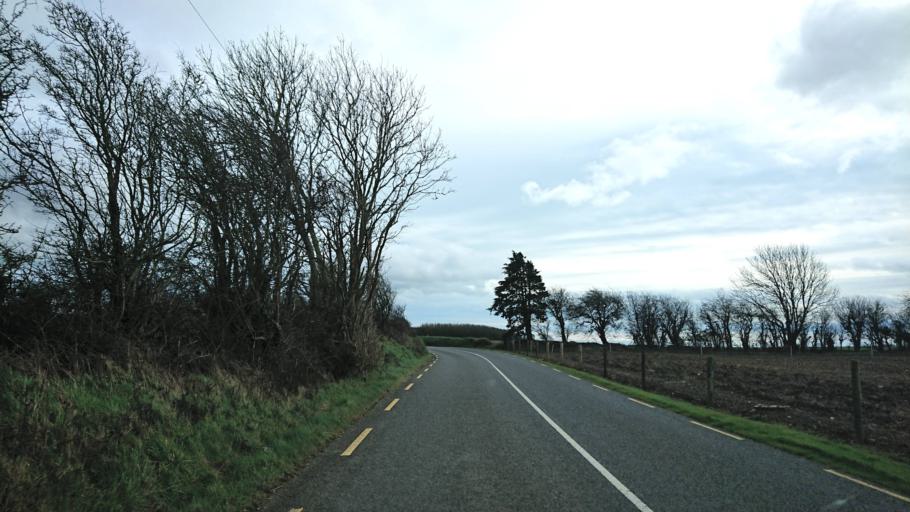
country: IE
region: Munster
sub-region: Waterford
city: Dunmore East
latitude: 52.2448
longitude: -6.8999
